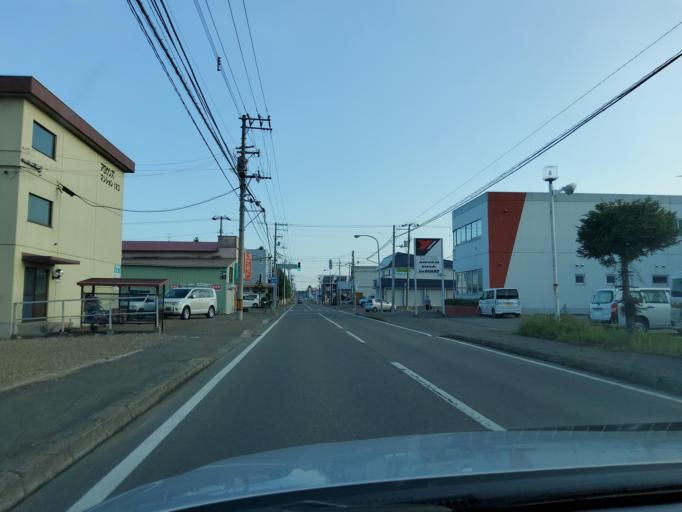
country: JP
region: Hokkaido
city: Obihiro
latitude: 42.9336
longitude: 143.1833
